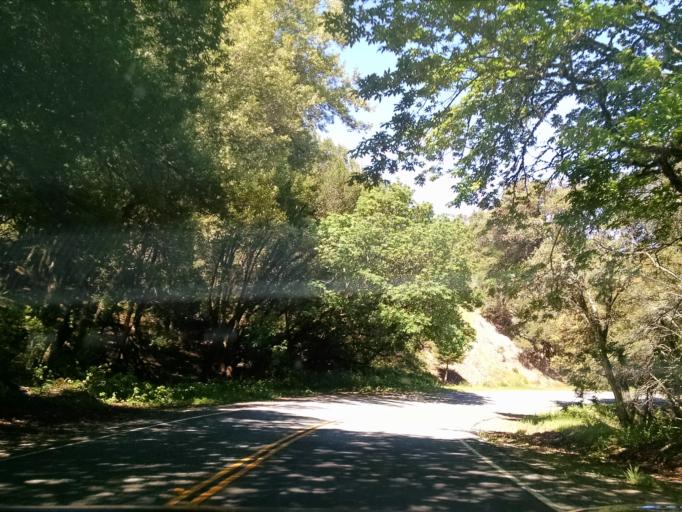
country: US
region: California
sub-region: San Mateo County
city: Portola Valley
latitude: 37.3351
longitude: -122.2166
